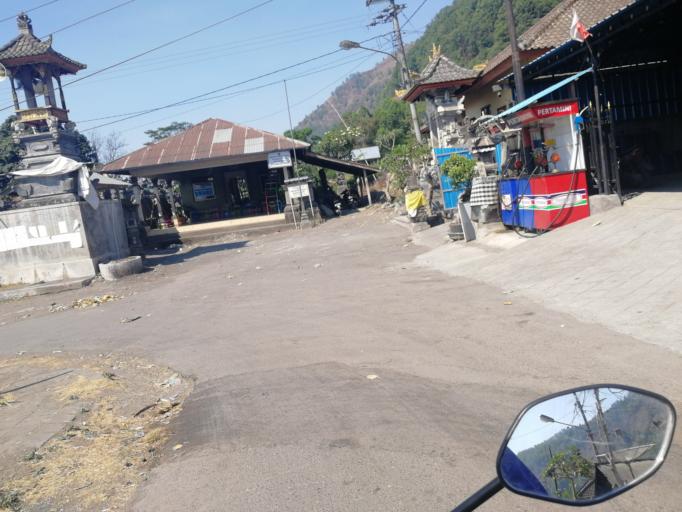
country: ID
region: Bali
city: Banjar Trunyan
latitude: -8.2743
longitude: 115.4143
